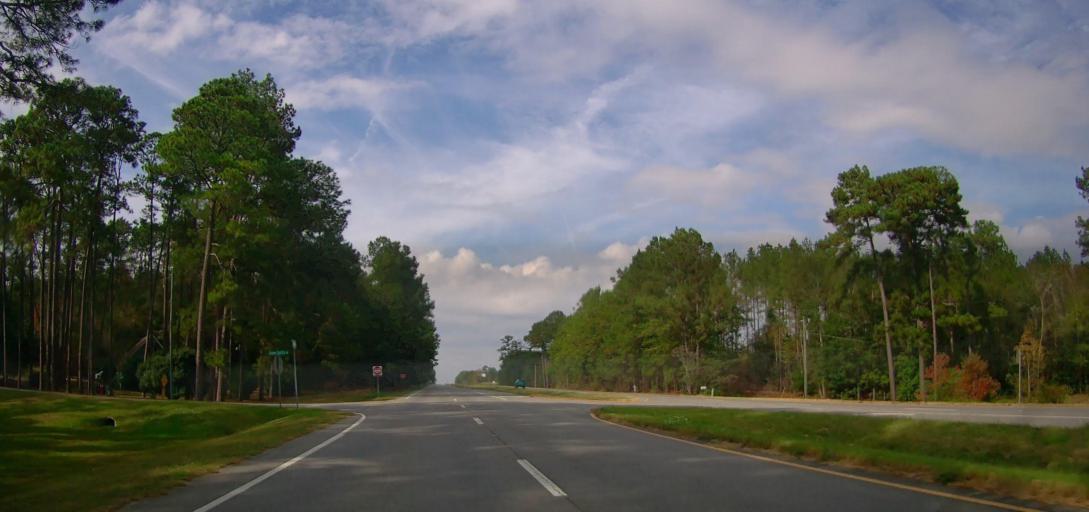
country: US
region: Georgia
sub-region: Thomas County
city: Meigs
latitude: 30.9697
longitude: -84.0337
